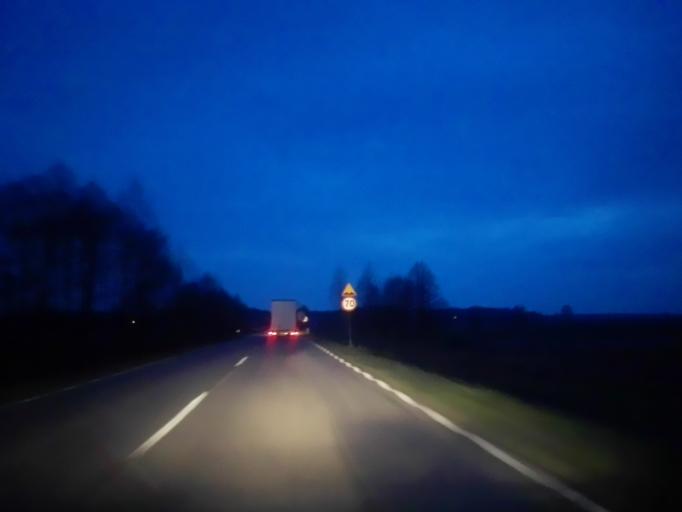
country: PL
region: Podlasie
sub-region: Powiat lomzynski
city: Sniadowo
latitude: 53.0347
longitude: 21.9786
